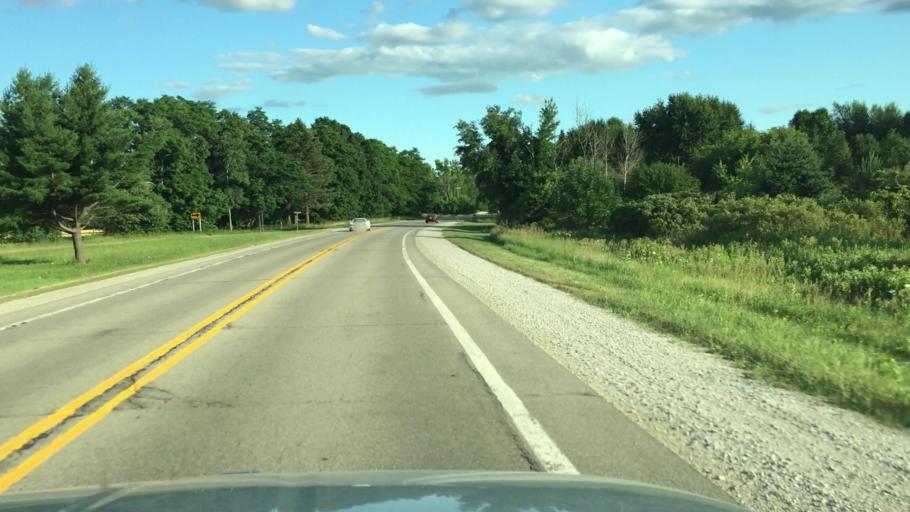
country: US
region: Michigan
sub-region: Saint Clair County
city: Yale
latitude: 43.0618
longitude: -82.7652
